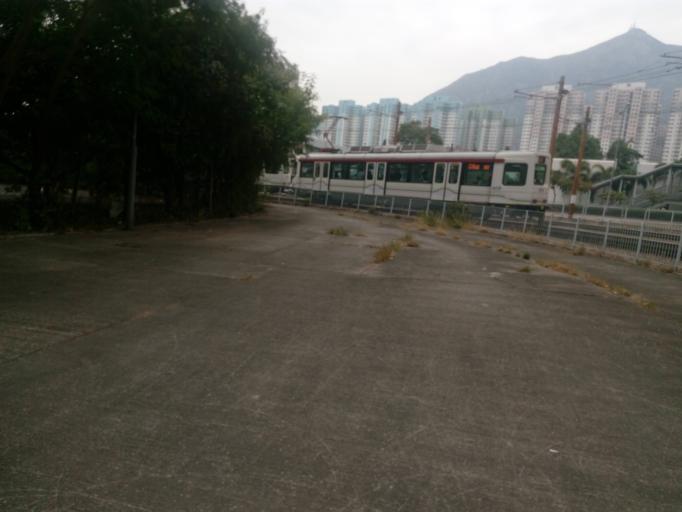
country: HK
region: Tuen Mun
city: Tuen Mun
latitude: 22.3834
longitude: 113.9710
